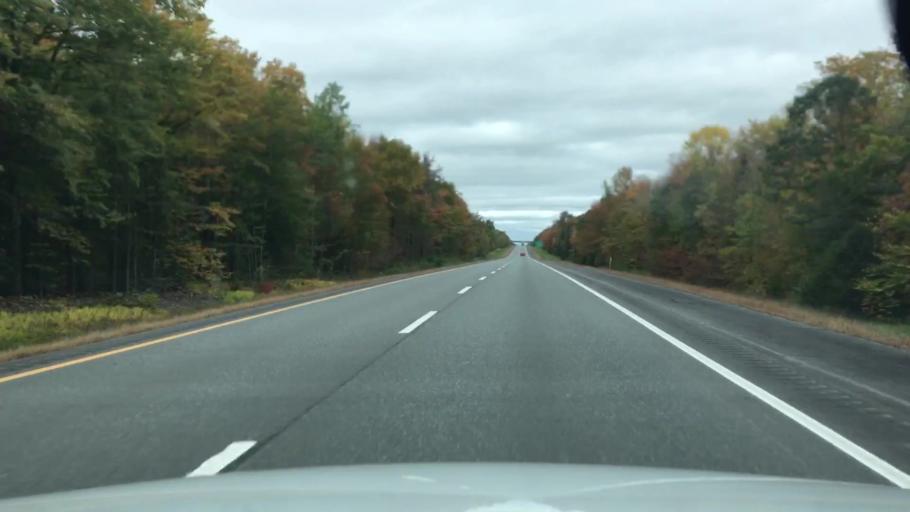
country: US
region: Maine
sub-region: Waldo County
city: Burnham
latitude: 44.7265
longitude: -69.4383
